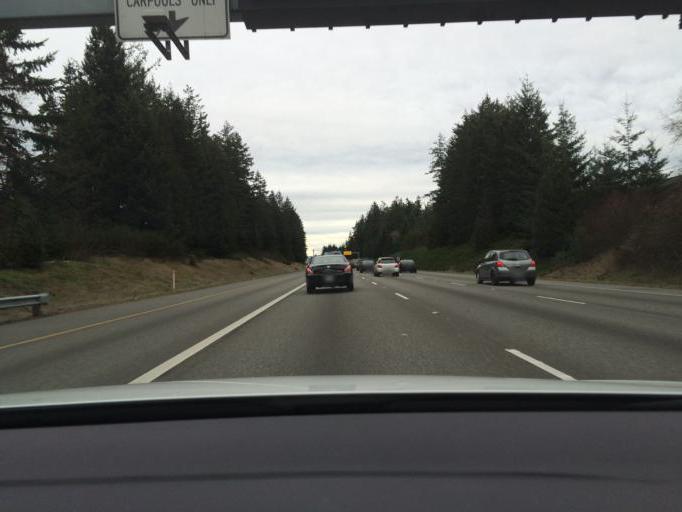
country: US
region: Washington
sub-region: Snohomish County
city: Mill Creek
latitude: 47.8908
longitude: -122.2215
